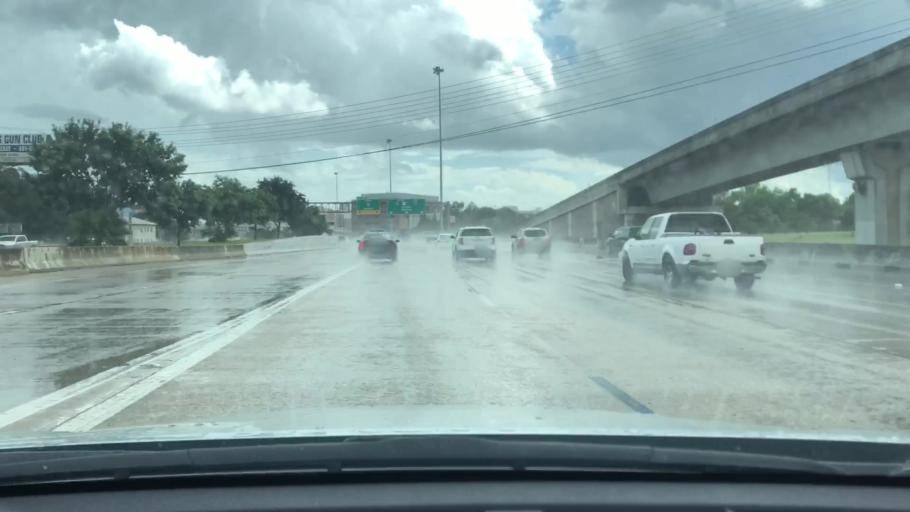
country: US
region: Texas
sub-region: Bexar County
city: San Antonio
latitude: 29.4372
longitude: -98.5046
